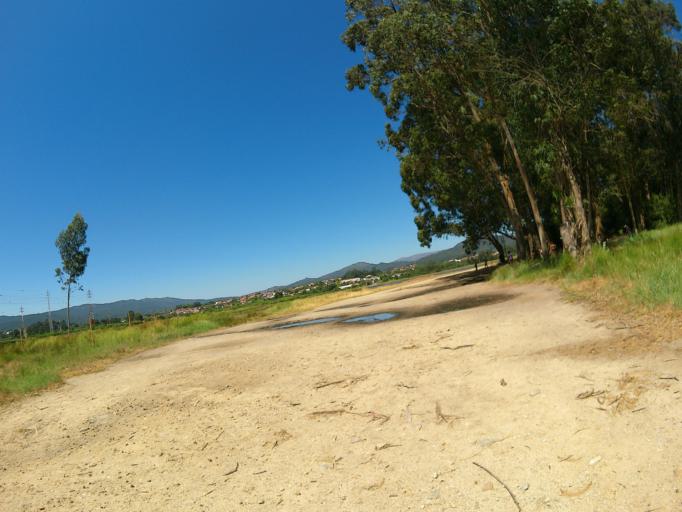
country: PT
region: Viana do Castelo
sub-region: Viana do Castelo
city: Darque
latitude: 41.6925
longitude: -8.7732
